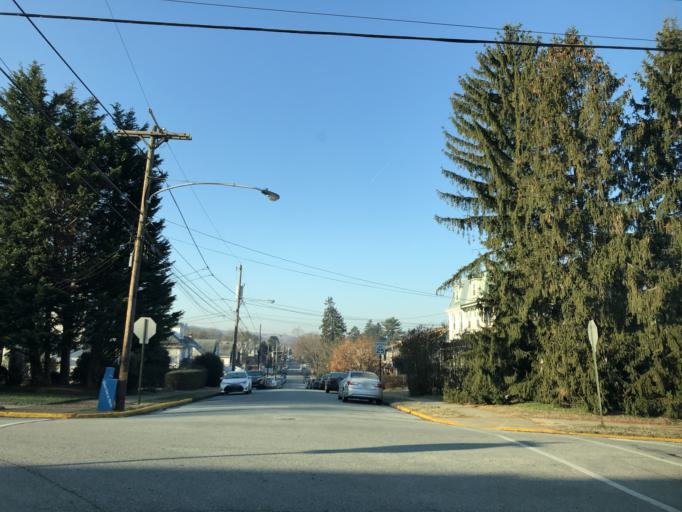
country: US
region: Pennsylvania
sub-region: Chester County
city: Downingtown
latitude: 40.0023
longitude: -75.7143
